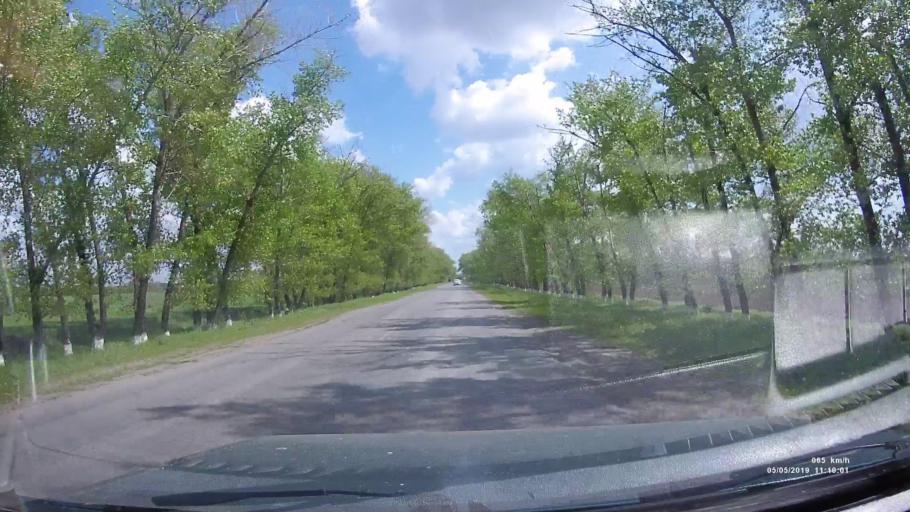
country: RU
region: Rostov
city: Ust'-Donetskiy
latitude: 47.7427
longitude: 40.9327
